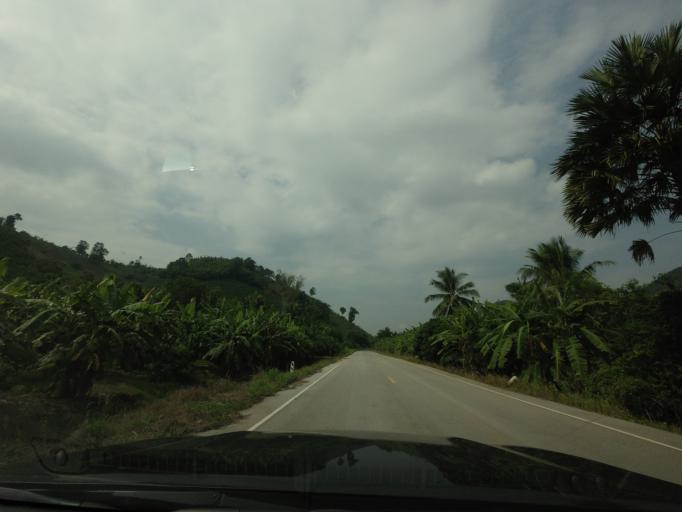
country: LA
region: Xiagnabouli
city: Muang Kenthao
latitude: 17.7696
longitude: 101.5189
